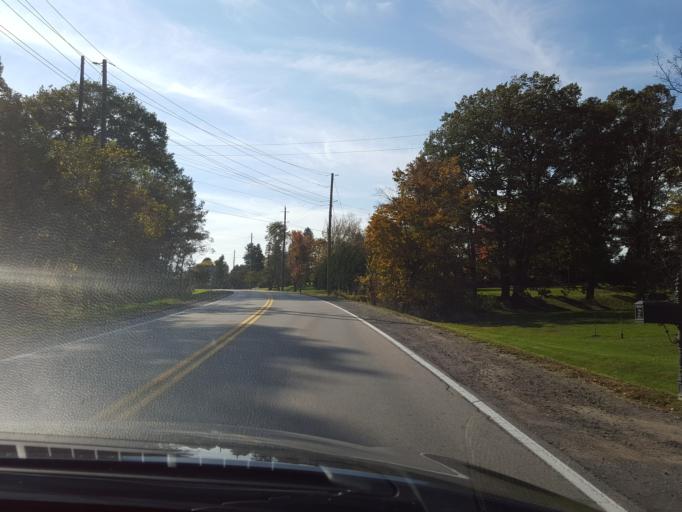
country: CA
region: Ontario
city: Ancaster
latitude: 43.2545
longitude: -80.0015
